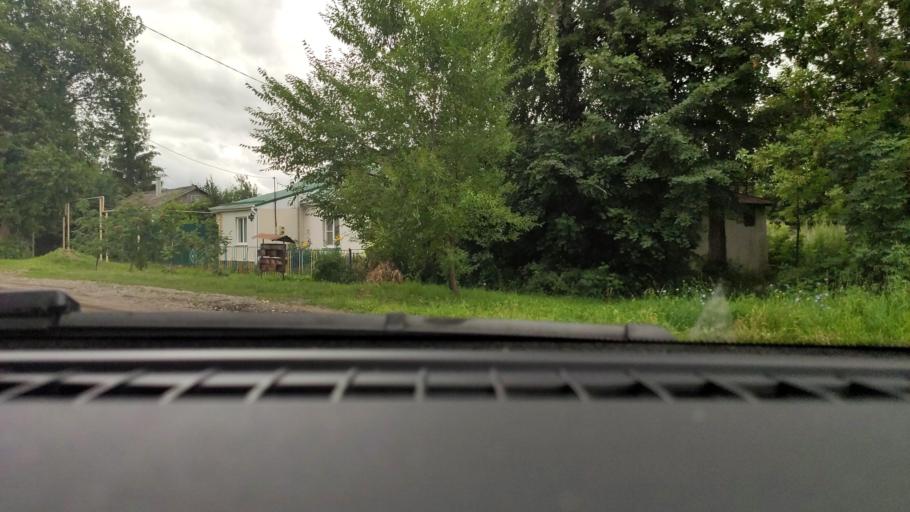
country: RU
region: Voronezj
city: Zemlyansk
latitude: 51.9065
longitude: 38.7260
